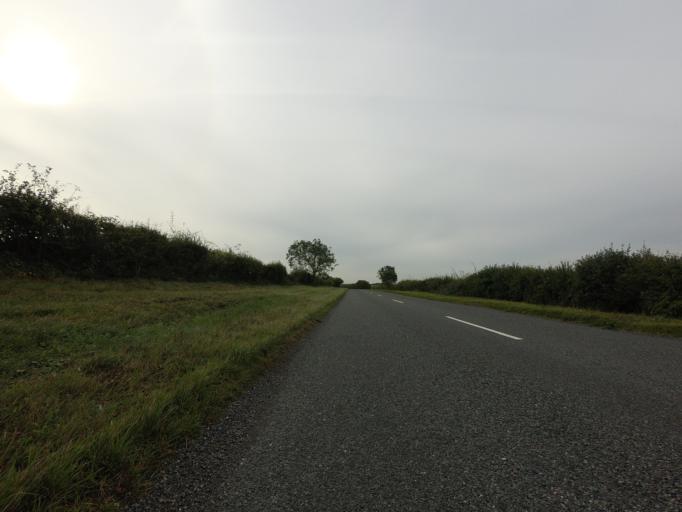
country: GB
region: England
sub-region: Cambridgeshire
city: Melbourn
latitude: 52.0480
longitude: 0.0458
